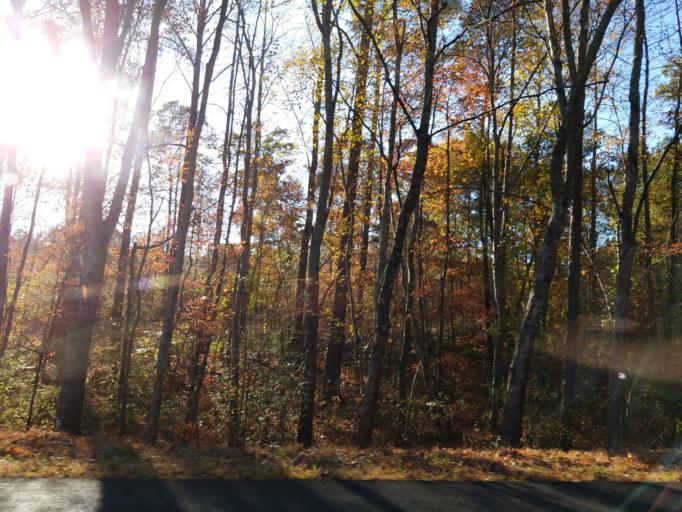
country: US
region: Georgia
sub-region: Gilmer County
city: Ellijay
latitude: 34.6039
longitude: -84.4638
